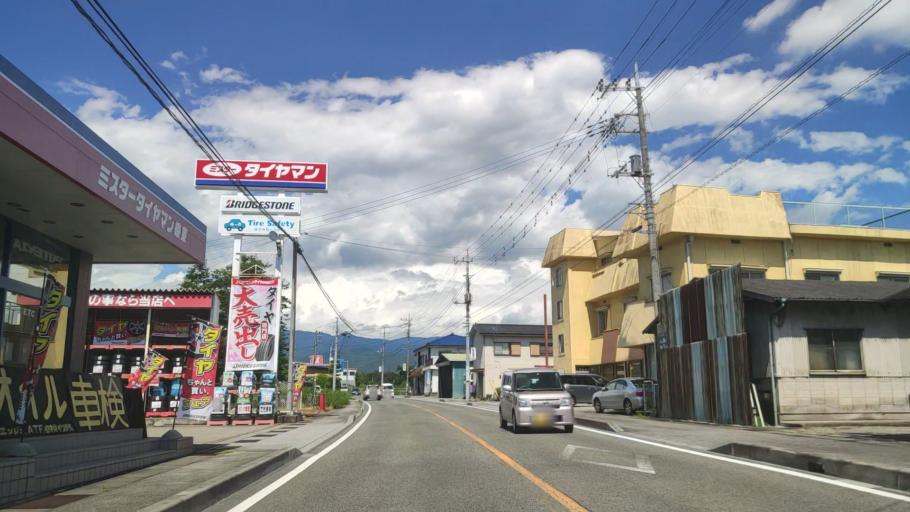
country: JP
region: Yamanashi
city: Enzan
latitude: 35.6998
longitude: 138.6890
